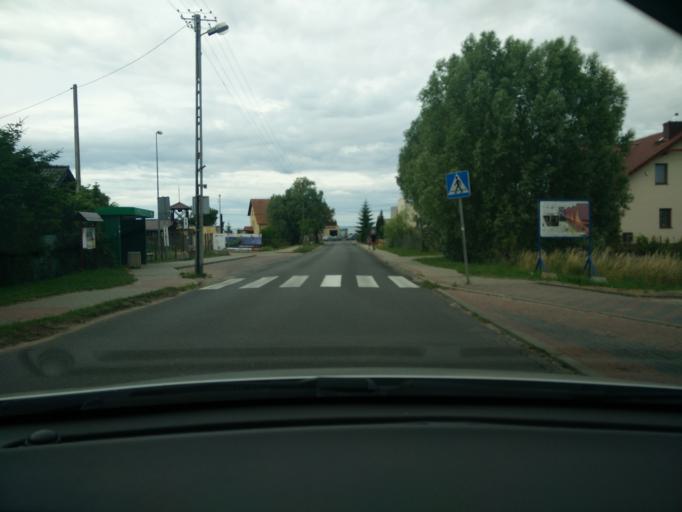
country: PL
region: Pomeranian Voivodeship
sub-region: Powiat pucki
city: Mosty
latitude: 54.6304
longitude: 18.4969
